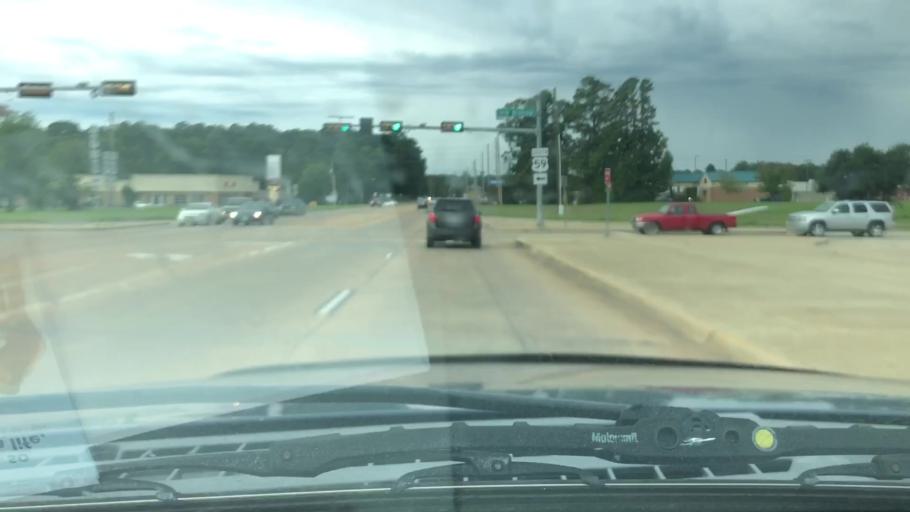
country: US
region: Texas
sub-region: Bowie County
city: Wake Village
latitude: 33.4435
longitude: -94.0971
